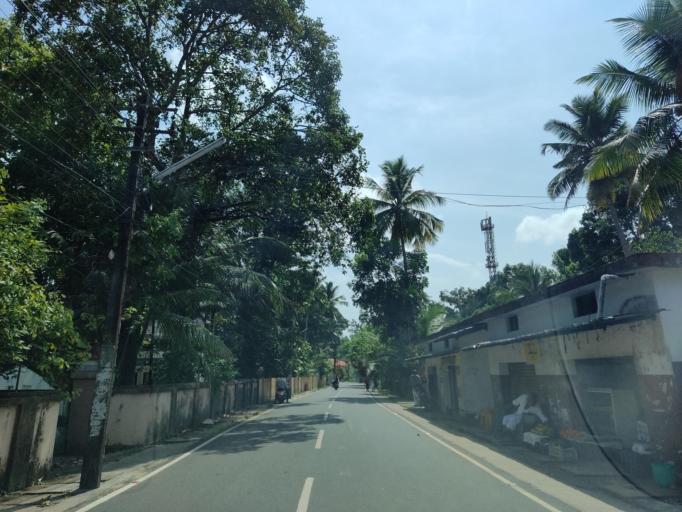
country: IN
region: Kerala
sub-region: Alappuzha
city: Mavelikara
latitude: 9.3195
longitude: 76.5322
